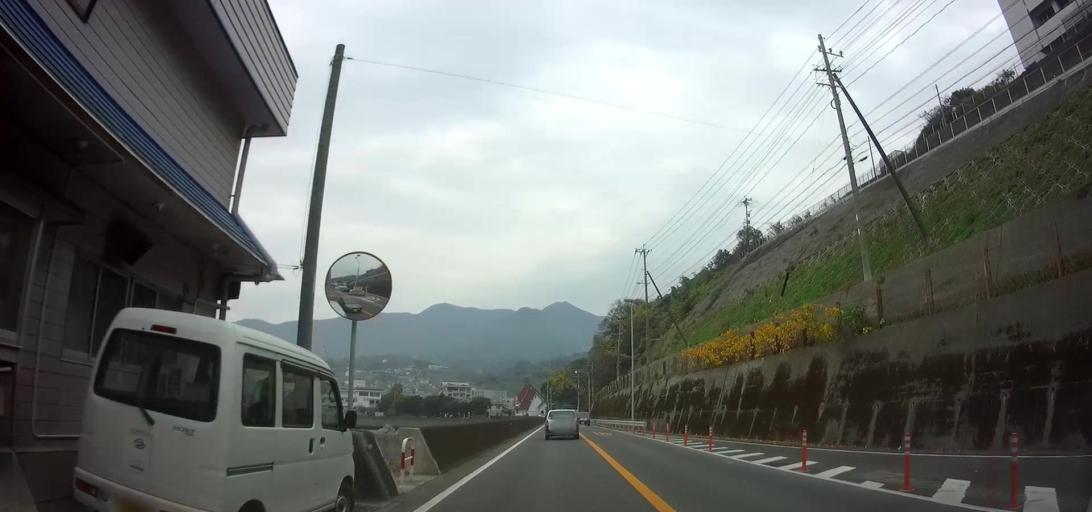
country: JP
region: Nagasaki
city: Shimabara
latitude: 32.7171
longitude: 130.1973
